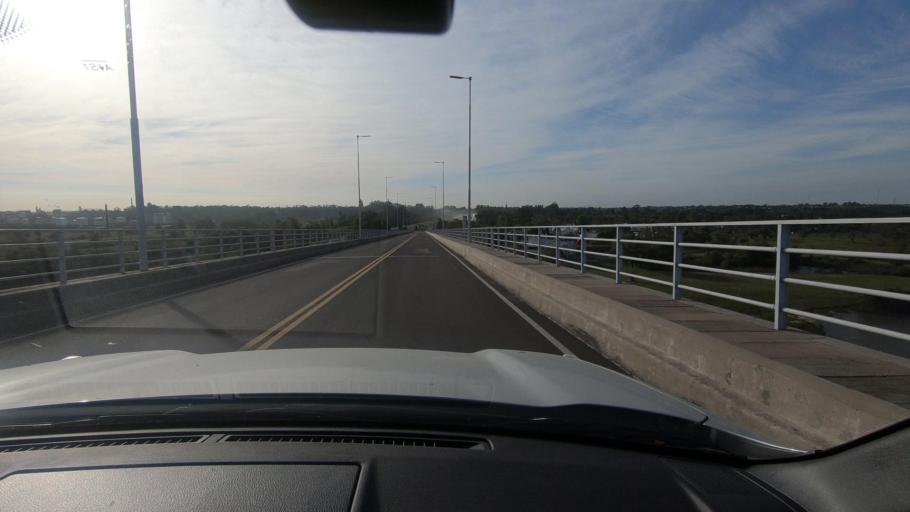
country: AR
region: Entre Rios
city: Colon
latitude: -32.2424
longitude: -58.1516
